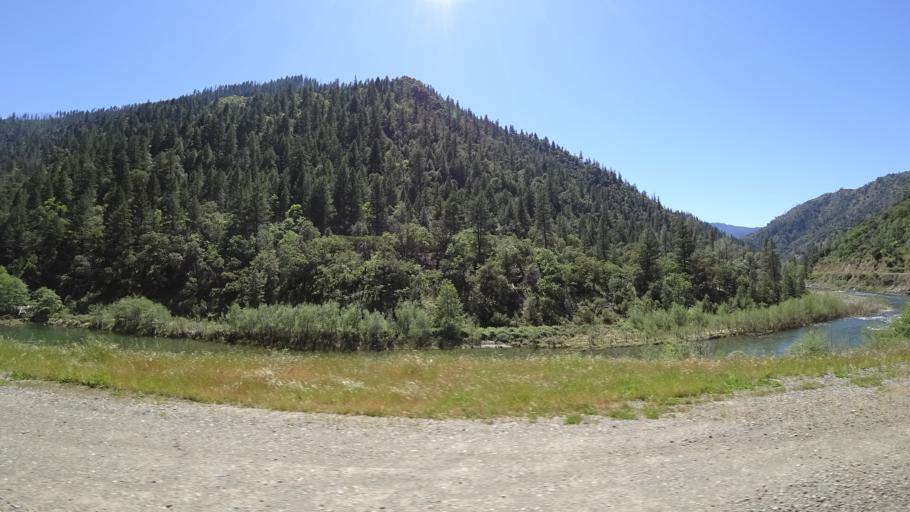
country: US
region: California
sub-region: Humboldt County
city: Willow Creek
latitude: 40.8004
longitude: -123.3887
